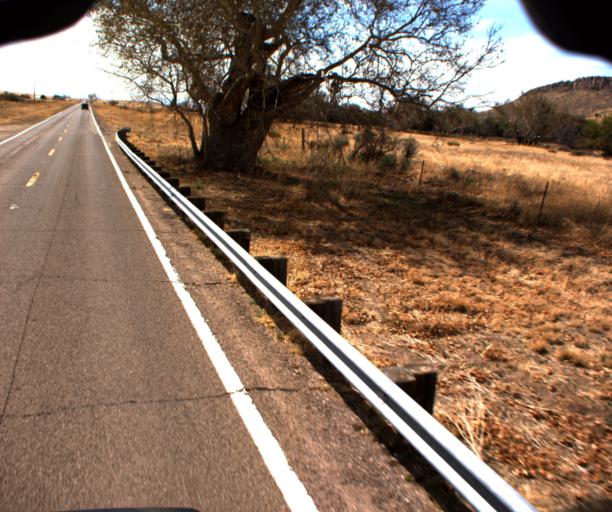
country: US
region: Arizona
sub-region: Cochise County
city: Willcox
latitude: 32.0067
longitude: -109.3969
